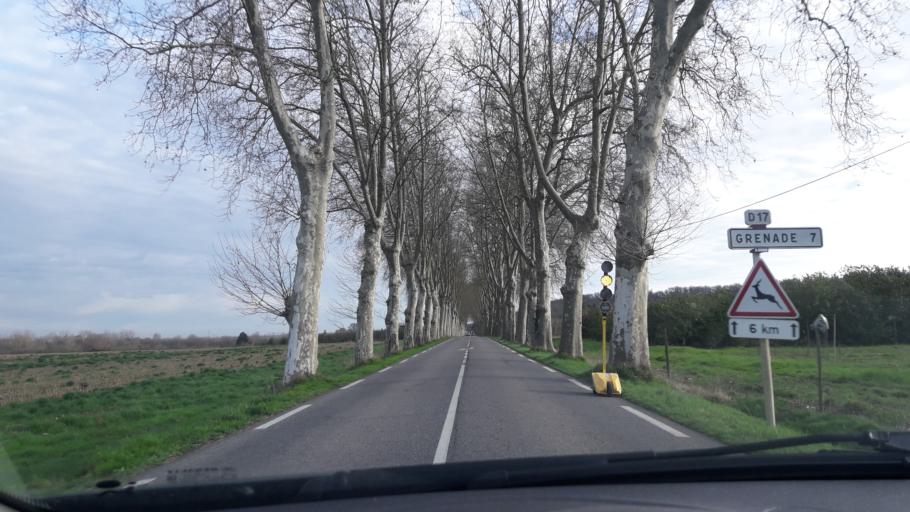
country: FR
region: Midi-Pyrenees
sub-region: Departement de la Haute-Garonne
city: Daux
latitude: 43.7253
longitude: 1.2478
